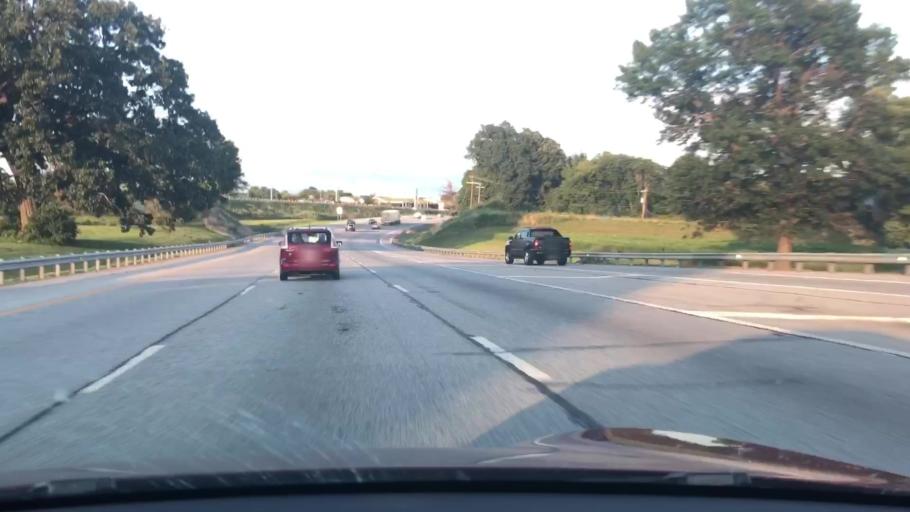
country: US
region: Delaware
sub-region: New Castle County
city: Wilmington Manor
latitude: 39.6953
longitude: -75.5732
